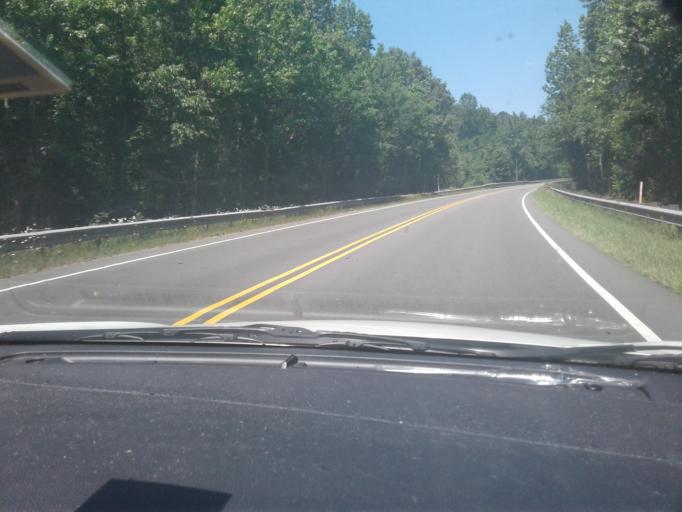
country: US
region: North Carolina
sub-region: Harnett County
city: Lillington
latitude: 35.4277
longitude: -78.8226
